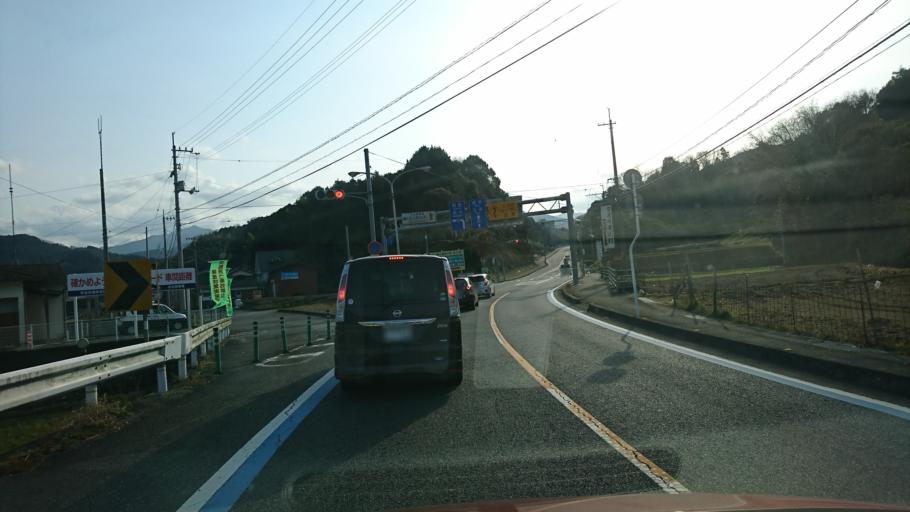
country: JP
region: Ehime
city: Hojo
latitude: 34.0024
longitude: 132.9380
